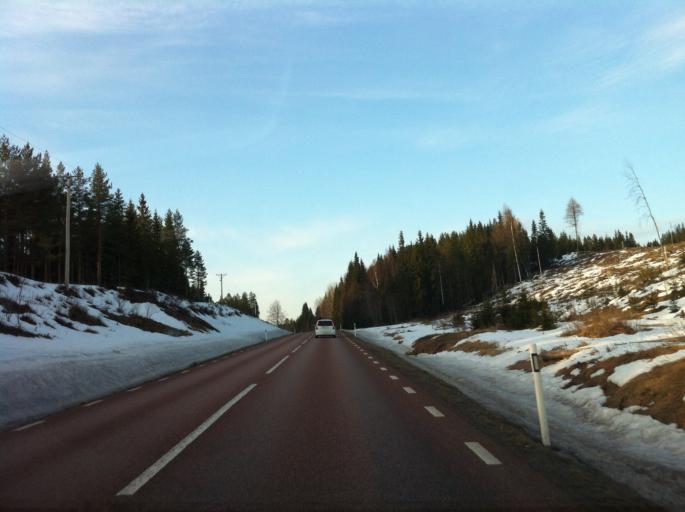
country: SE
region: Dalarna
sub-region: Vansbro Kommun
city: Vansbro
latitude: 60.2629
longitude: 14.1725
